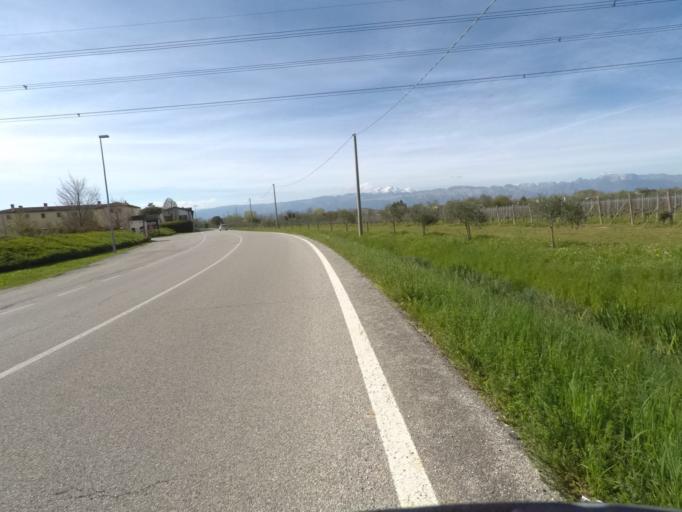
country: IT
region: Friuli Venezia Giulia
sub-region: Provincia di Pordenone
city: Fiume Veneto
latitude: 45.9353
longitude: 12.7101
